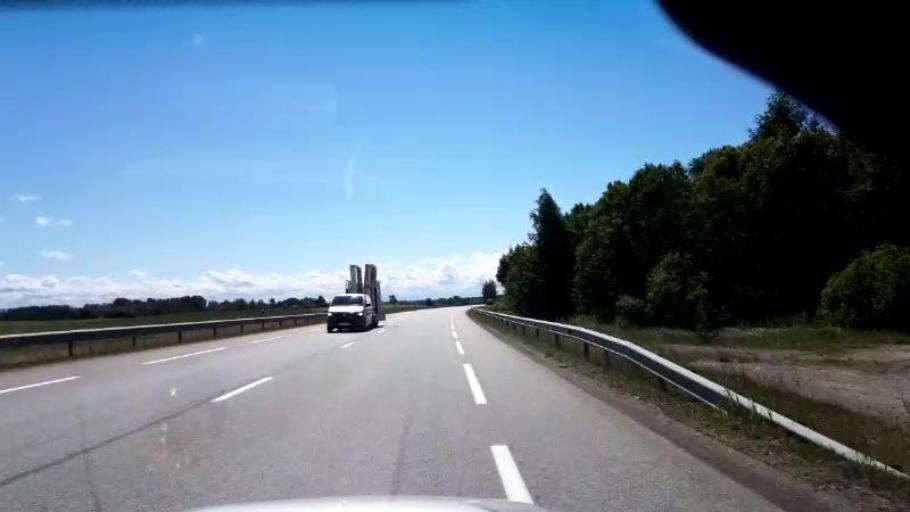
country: LV
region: Saulkrastu
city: Saulkrasti
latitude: 57.4102
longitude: 24.4320
